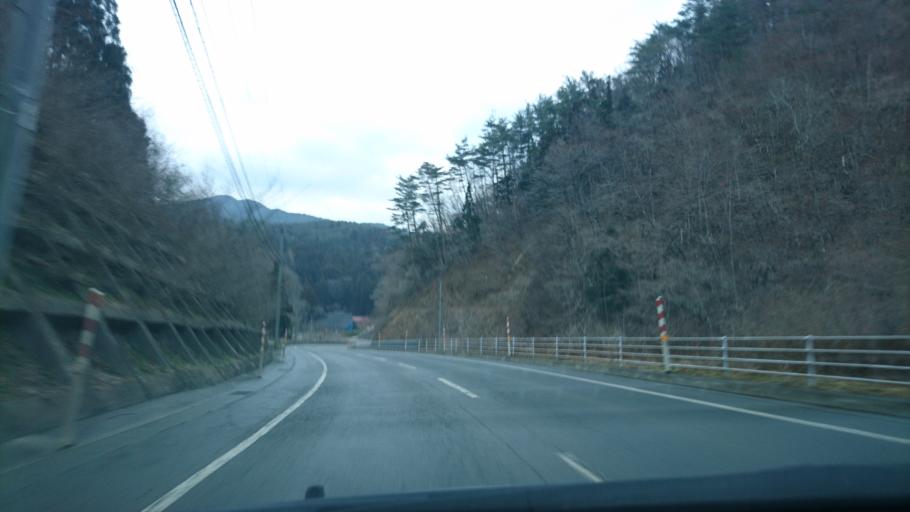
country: JP
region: Iwate
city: Ofunato
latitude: 39.0193
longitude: 141.5479
